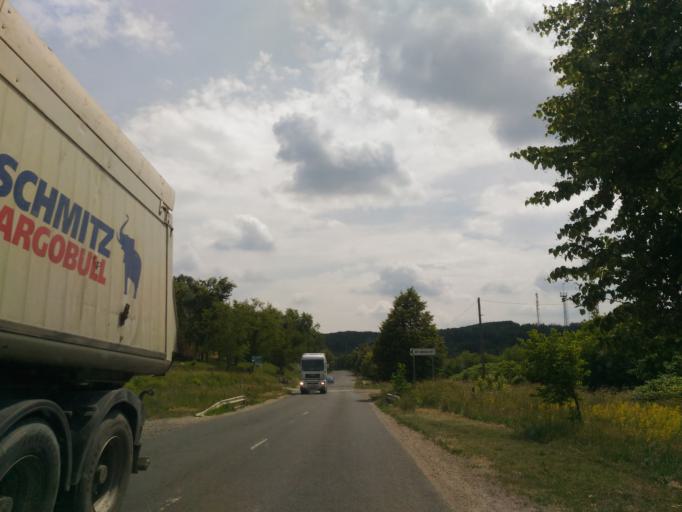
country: HU
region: Baranya
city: Komlo
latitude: 46.1981
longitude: 18.2524
